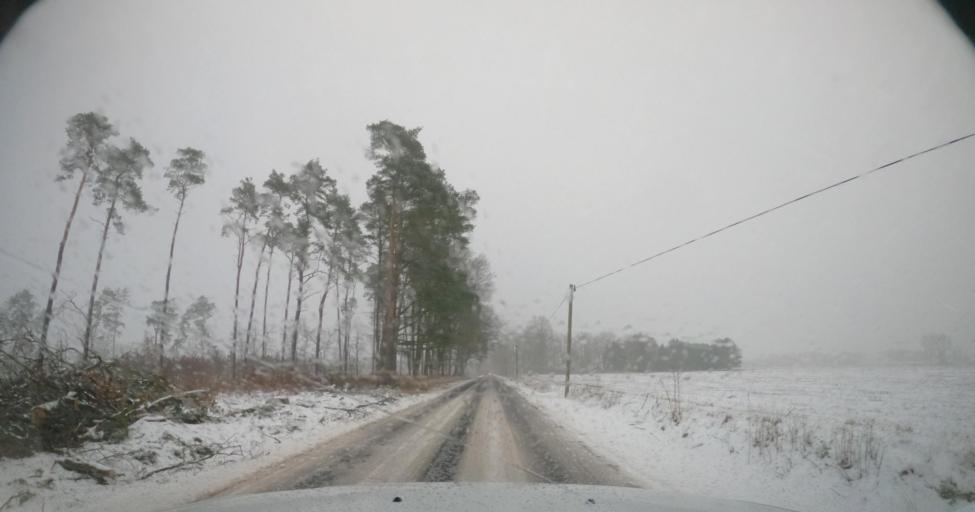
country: PL
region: West Pomeranian Voivodeship
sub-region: Powiat goleniowski
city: Przybiernow
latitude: 53.6885
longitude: 14.8471
